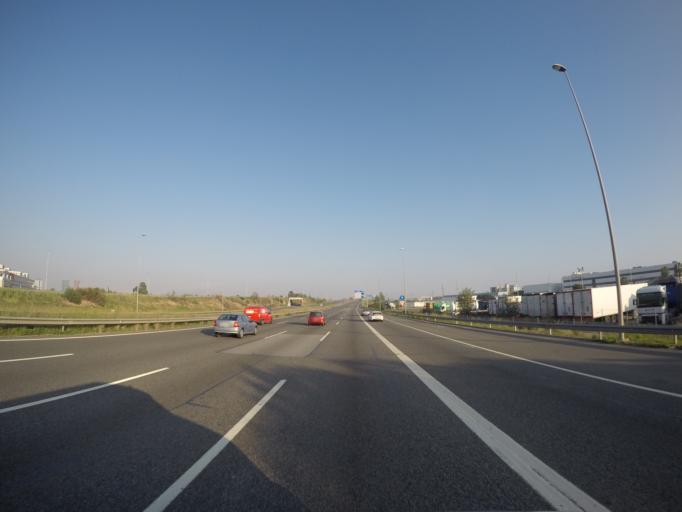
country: ES
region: Catalonia
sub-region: Provincia de Barcelona
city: El Prat de Llobregat
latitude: 41.3404
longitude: 2.1076
